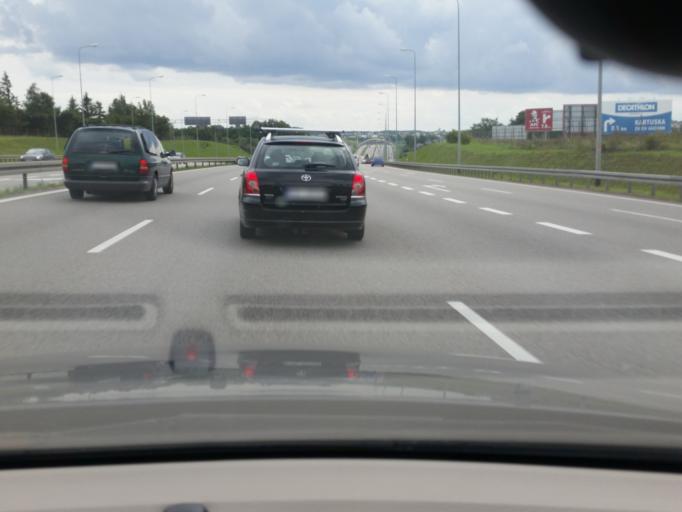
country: PL
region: Pomeranian Voivodeship
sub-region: Powiat gdanski
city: Kowale
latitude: 54.3645
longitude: 18.5194
